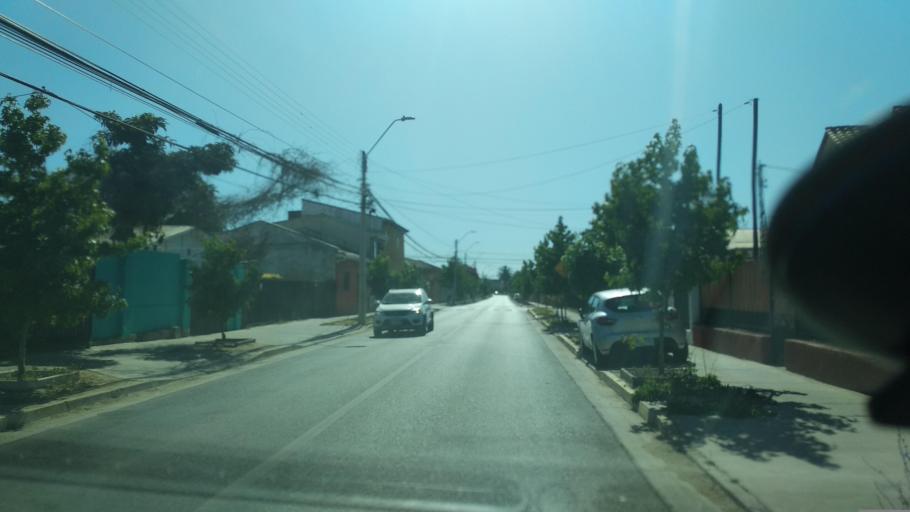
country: CL
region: Valparaiso
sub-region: Provincia de Marga Marga
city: Villa Alemana
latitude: -33.0432
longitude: -71.3810
